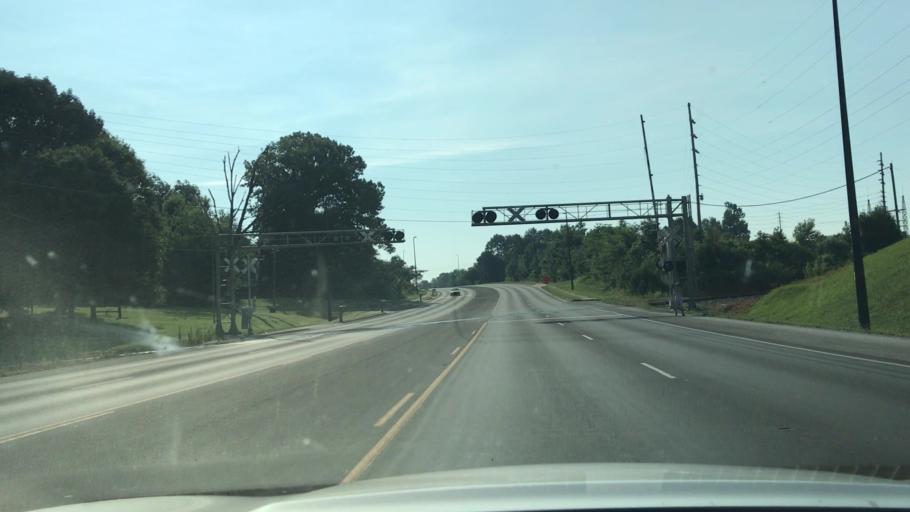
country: US
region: Kentucky
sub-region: Barren County
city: Glasgow
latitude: 37.0107
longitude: -85.9485
